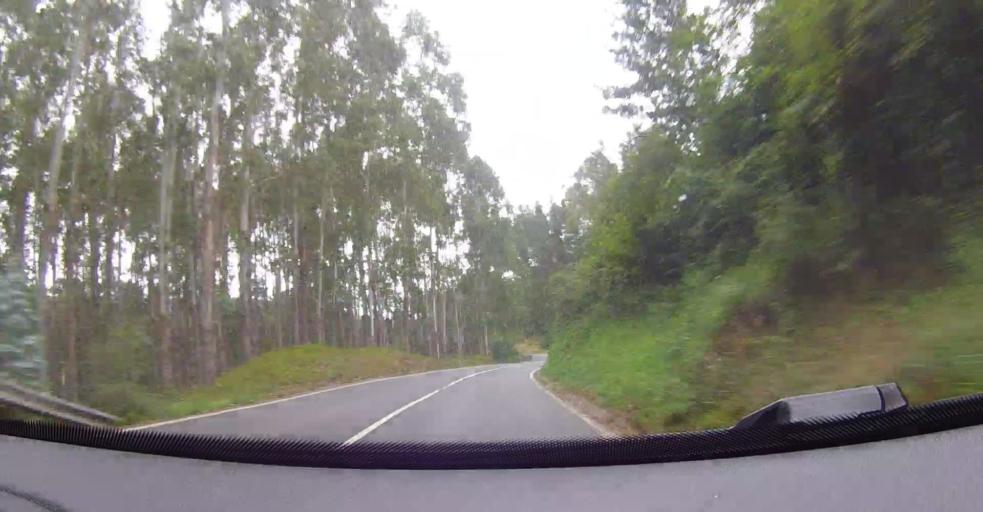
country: ES
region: Basque Country
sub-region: Bizkaia
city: Balmaseda
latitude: 43.2415
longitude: -3.2237
